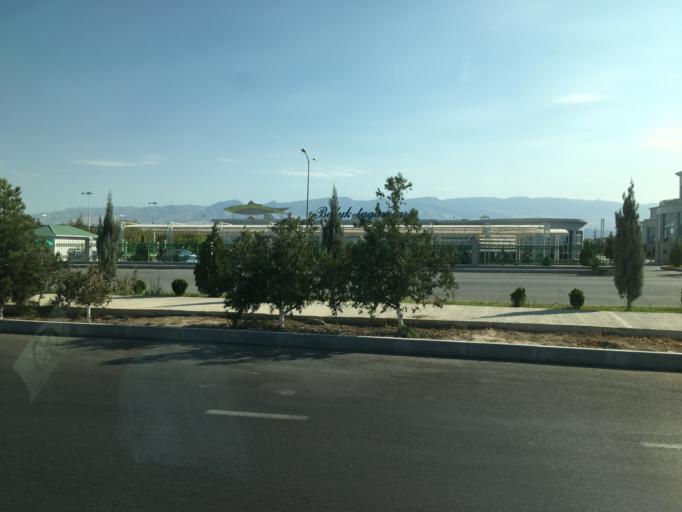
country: TM
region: Ahal
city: Ashgabat
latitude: 38.0121
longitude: 58.3358
